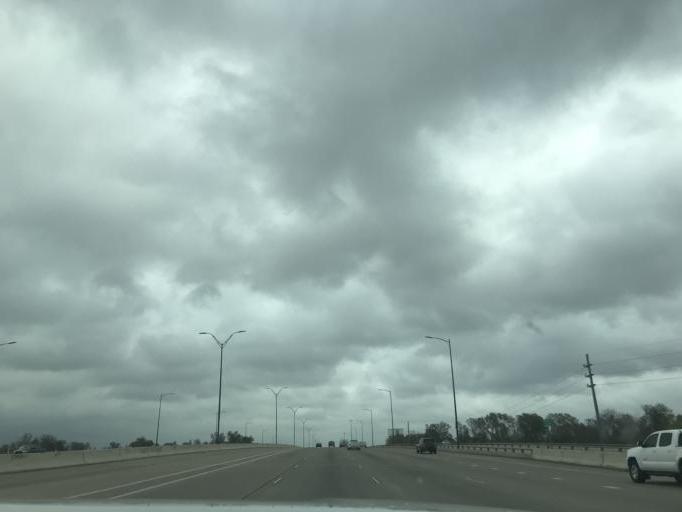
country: US
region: Texas
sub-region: Fort Bend County
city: Greatwood
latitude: 29.5667
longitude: -95.6704
